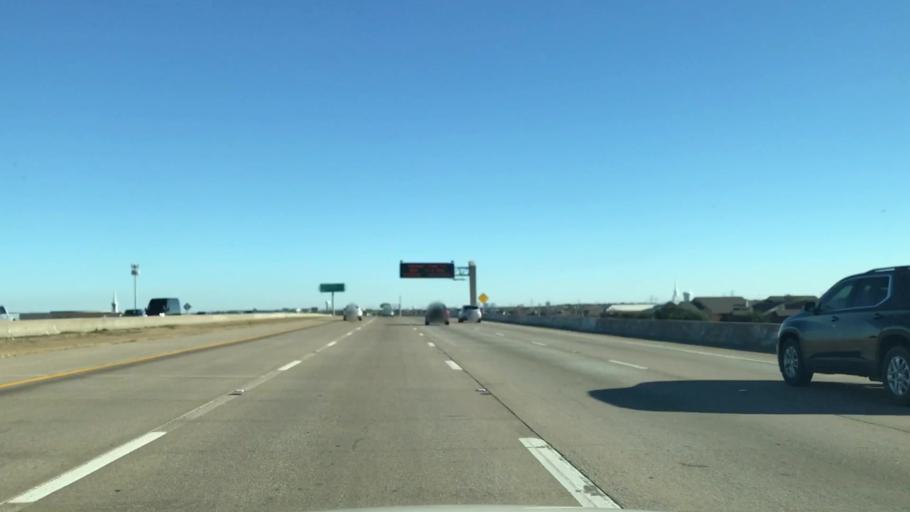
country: US
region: Texas
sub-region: Denton County
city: Lewisville
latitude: 33.0098
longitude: -96.9458
